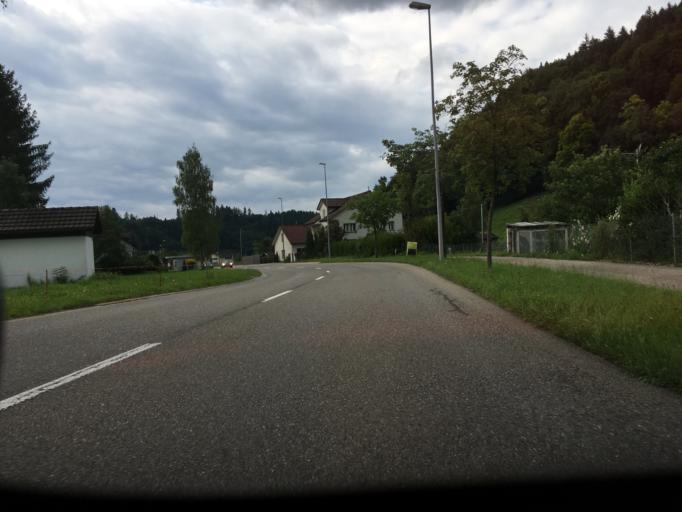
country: CH
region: Zurich
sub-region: Bezirk Pfaeffikon
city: Bauma
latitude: 47.3783
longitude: 8.8634
